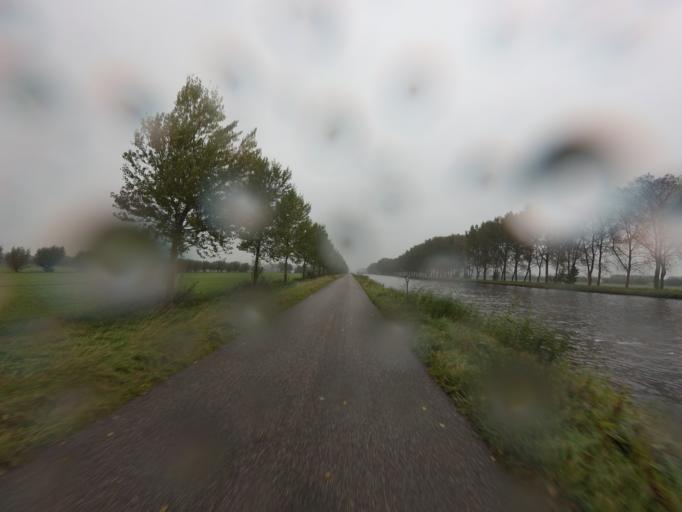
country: NL
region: South Holland
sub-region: Gemeente Leerdam
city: Leerdam
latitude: 51.9413
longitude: 5.0450
